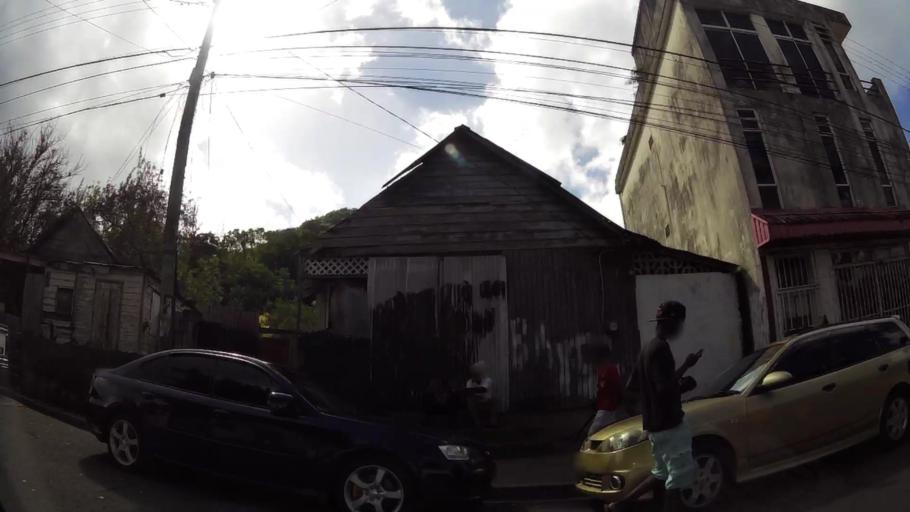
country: LC
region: Castries Quarter
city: Castries
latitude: 14.0059
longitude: -60.9878
